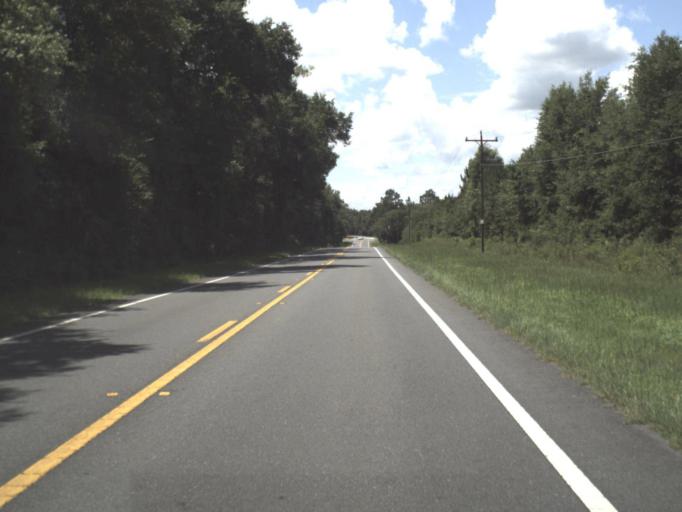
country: US
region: Florida
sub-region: Alachua County
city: Hawthorne
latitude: 29.6127
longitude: -82.0260
